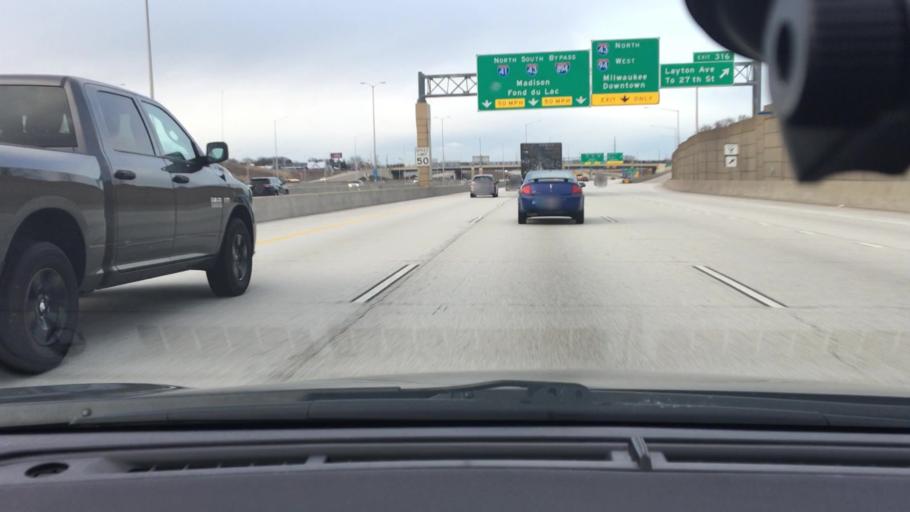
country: US
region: Wisconsin
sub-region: Milwaukee County
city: Saint Francis
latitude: 42.9543
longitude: -87.9346
